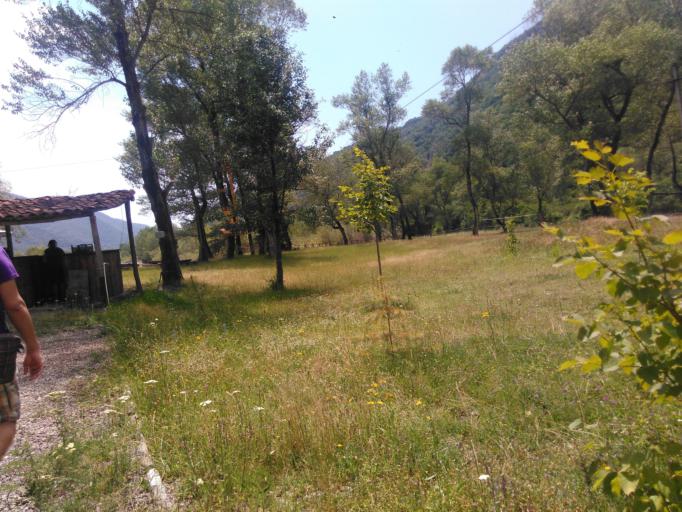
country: GE
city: Zhinvali
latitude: 42.2201
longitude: 44.8316
